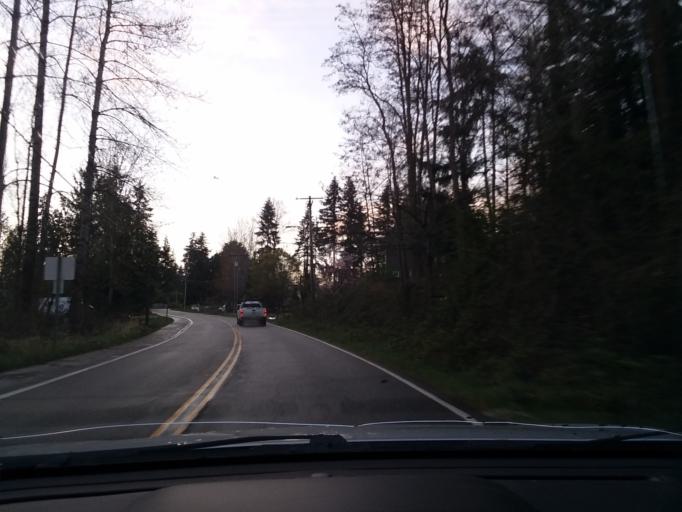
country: US
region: Washington
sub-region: King County
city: Kenmore
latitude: 47.7722
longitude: -122.2432
